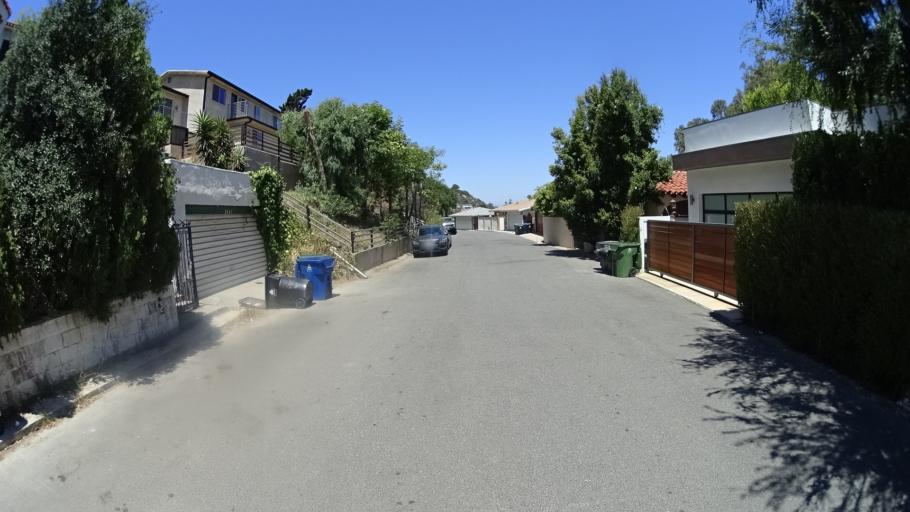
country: US
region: California
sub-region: Los Angeles County
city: Universal City
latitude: 34.1354
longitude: -118.3652
